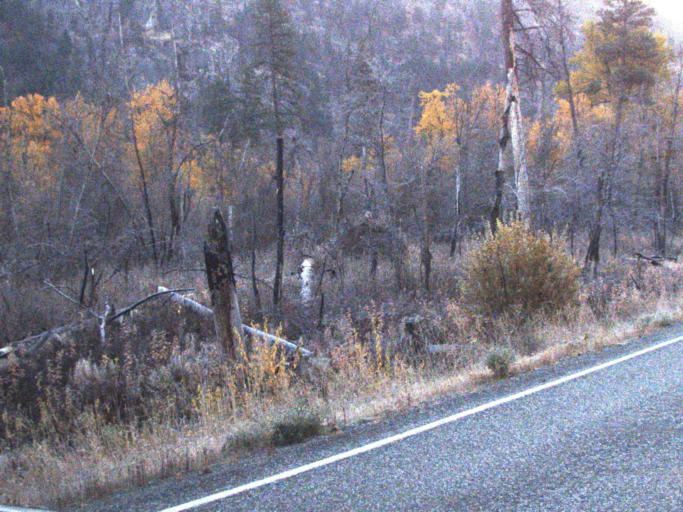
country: US
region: Washington
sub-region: Ferry County
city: Republic
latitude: 48.2853
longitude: -118.7251
